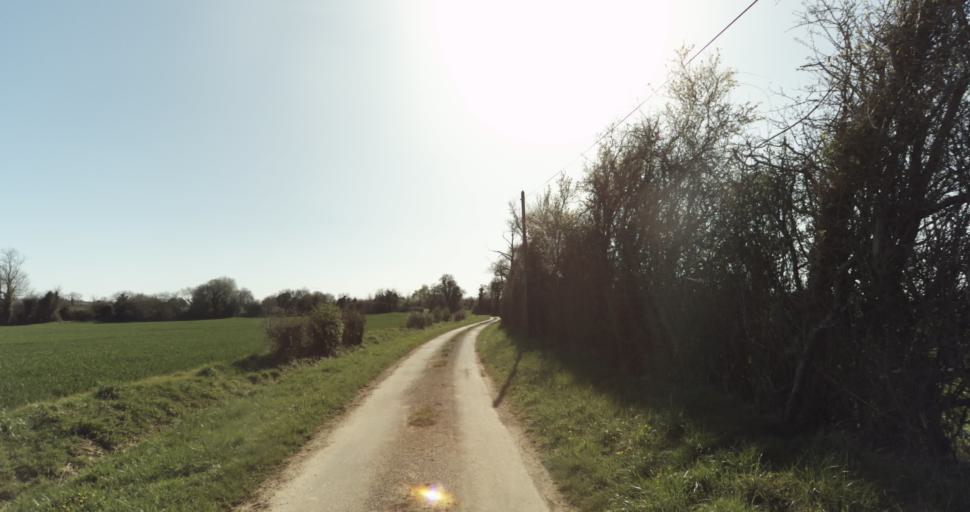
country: FR
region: Lower Normandy
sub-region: Departement de l'Orne
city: Trun
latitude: 48.9290
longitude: 0.0011
